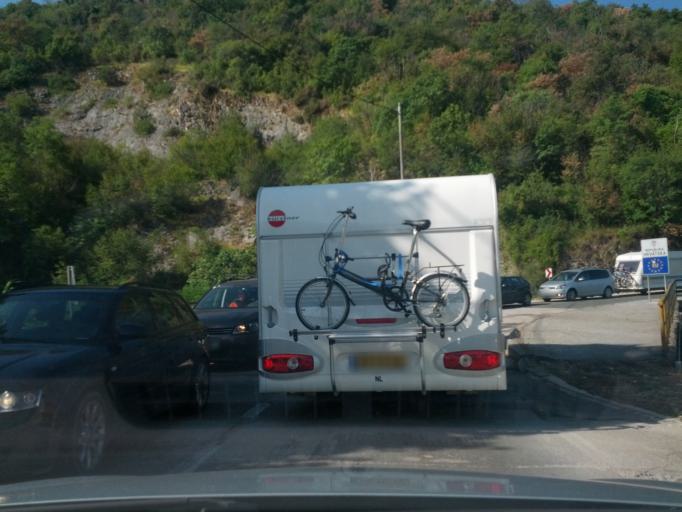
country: HR
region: Istarska
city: Buje
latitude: 45.4526
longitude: 13.6546
